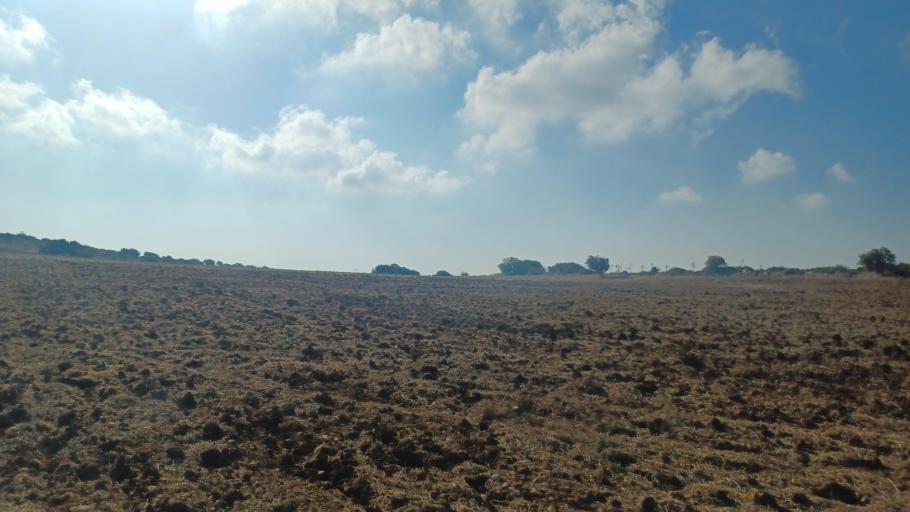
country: CY
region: Pafos
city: Mesogi
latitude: 34.7785
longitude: 32.4715
